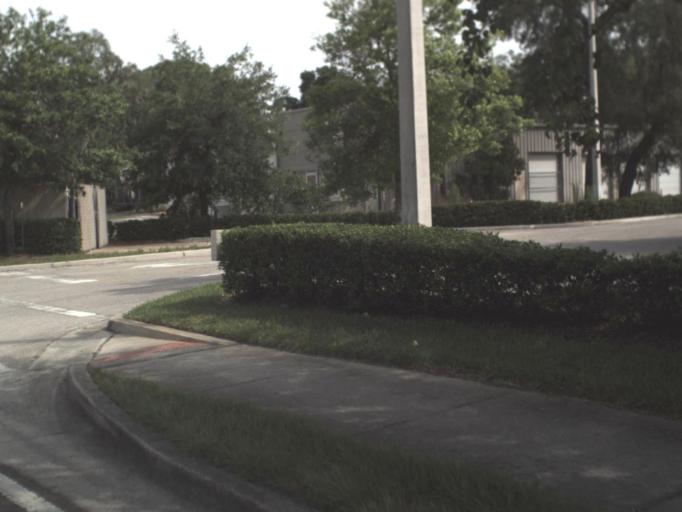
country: US
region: Florida
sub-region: Clay County
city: Green Cove Springs
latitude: 30.0025
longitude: -81.6852
